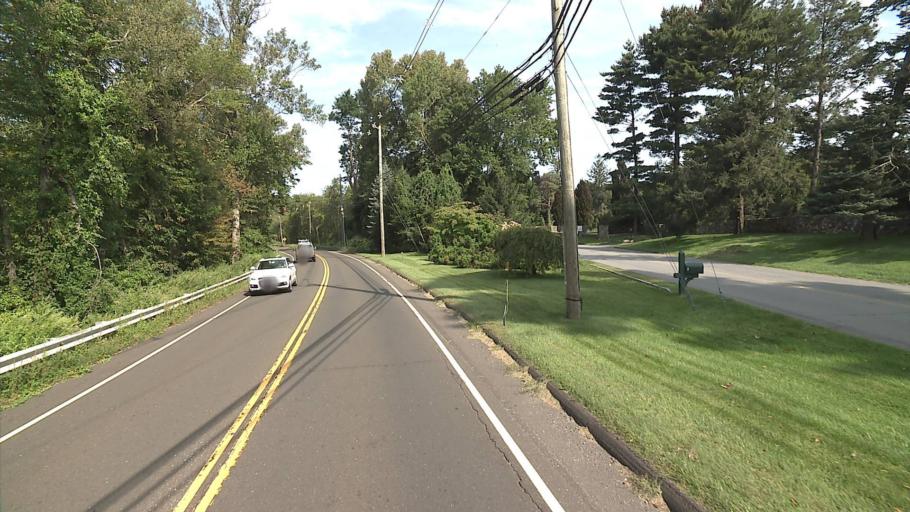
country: US
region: Connecticut
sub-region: Fairfield County
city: New Canaan
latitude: 41.1827
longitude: -73.5006
